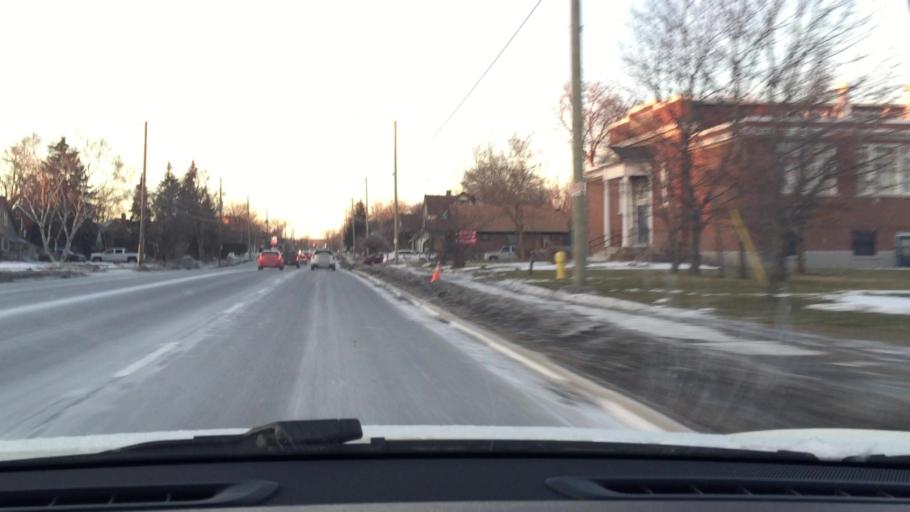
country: CA
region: Ontario
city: Oshawa
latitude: 43.9002
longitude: -78.8321
